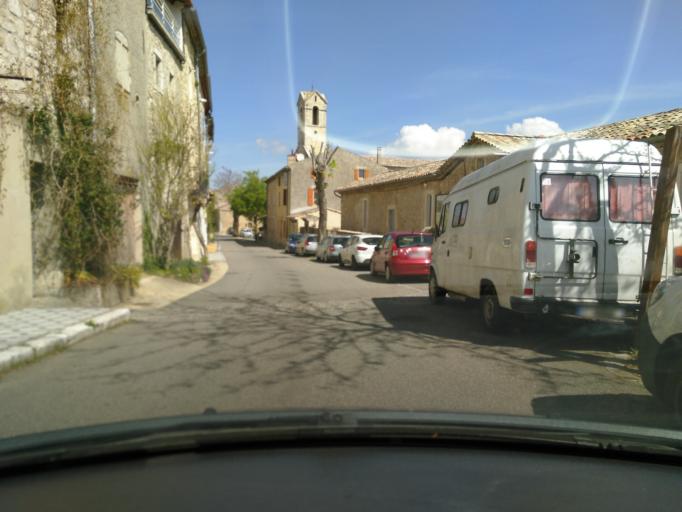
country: FR
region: Rhone-Alpes
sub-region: Departement de l'Ardeche
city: Ruoms
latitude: 44.4481
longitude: 4.4176
